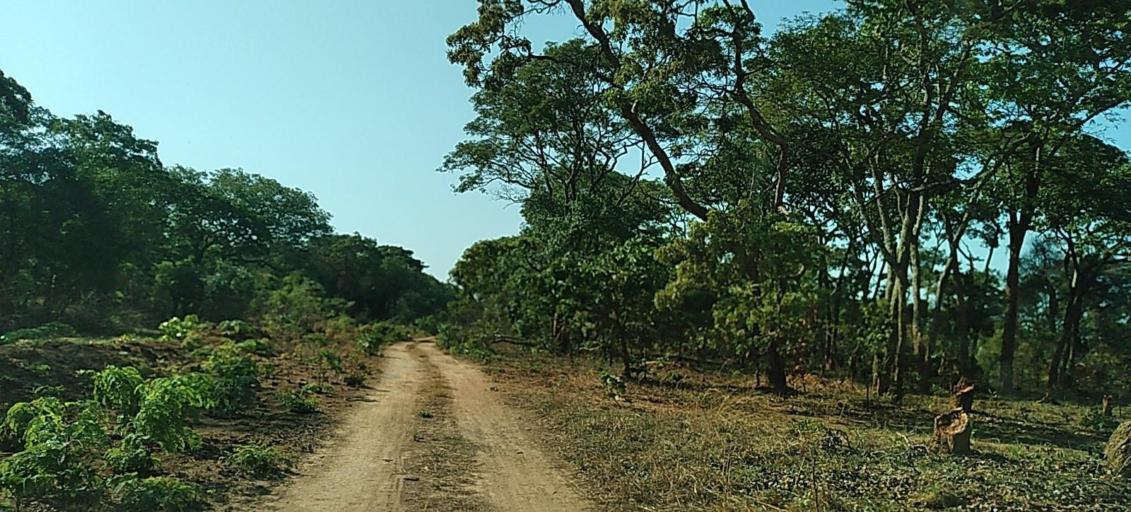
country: ZM
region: Central
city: Mkushi
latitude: -13.4576
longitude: 28.9100
